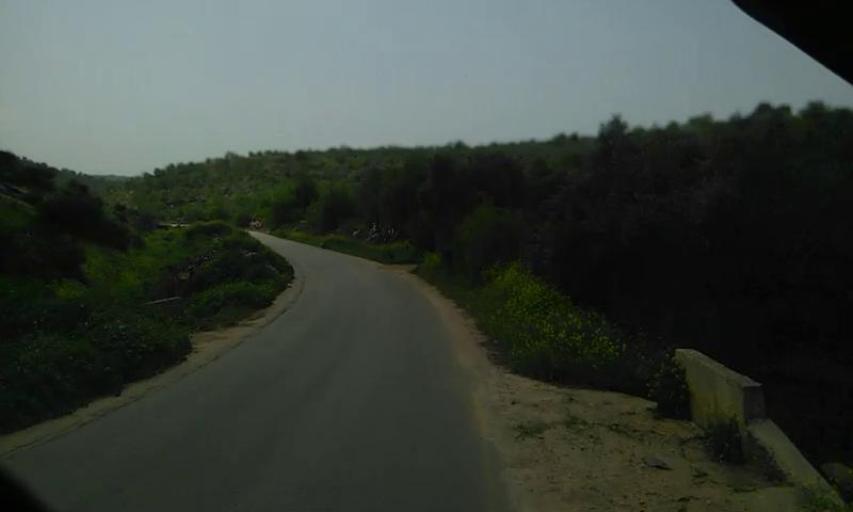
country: PS
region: West Bank
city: Rummanah
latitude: 32.5124
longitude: 35.2126
